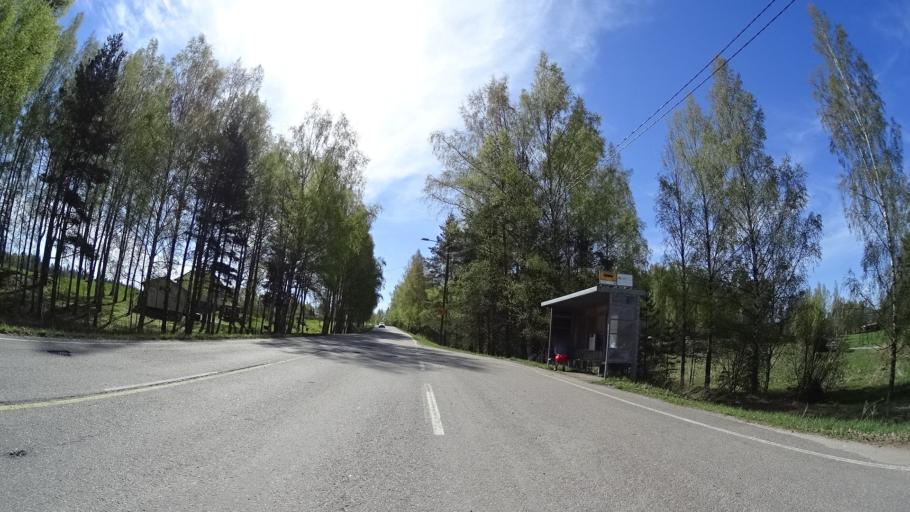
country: FI
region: Uusimaa
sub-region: Helsinki
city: Nurmijaervi
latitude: 60.3578
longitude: 24.8590
